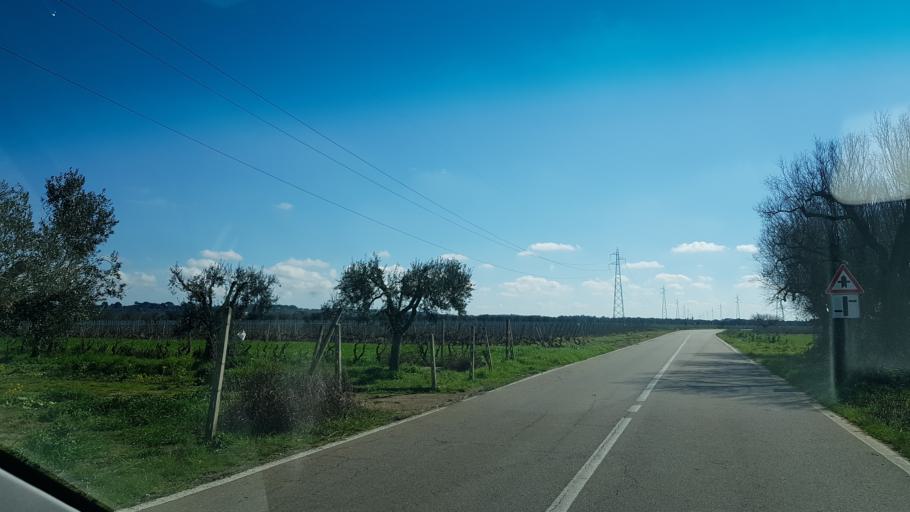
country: IT
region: Apulia
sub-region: Provincia di Lecce
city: Campi Salentina
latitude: 40.4276
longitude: 17.9977
